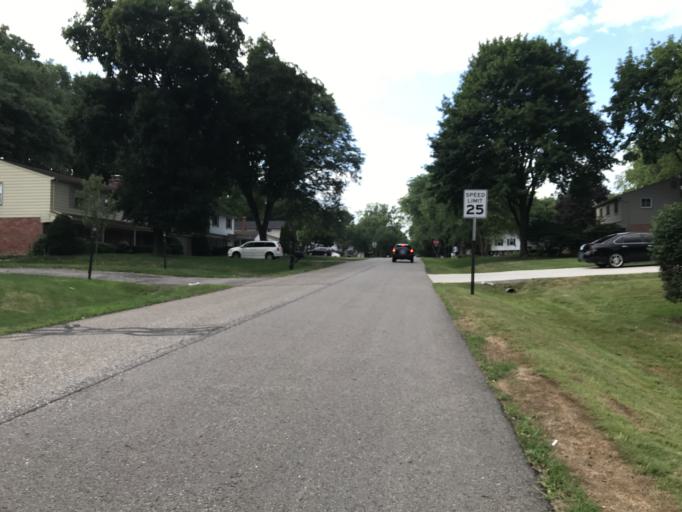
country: US
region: Michigan
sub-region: Oakland County
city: Farmington Hills
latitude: 42.4879
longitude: -83.3477
